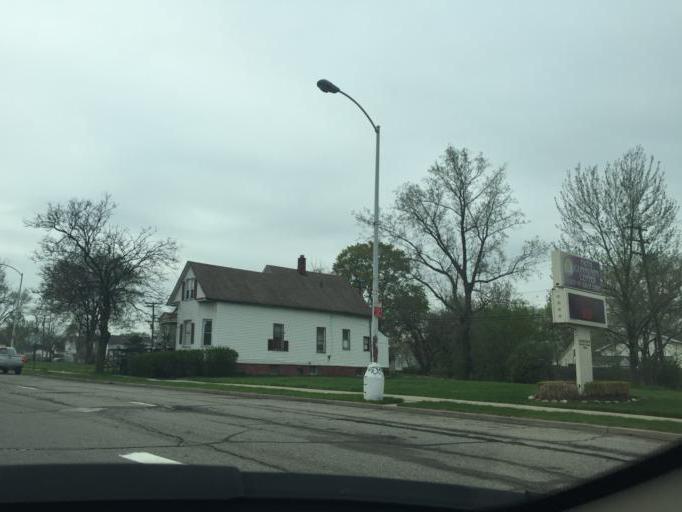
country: US
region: Michigan
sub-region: Wayne County
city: Detroit
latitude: 42.3371
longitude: -83.0918
